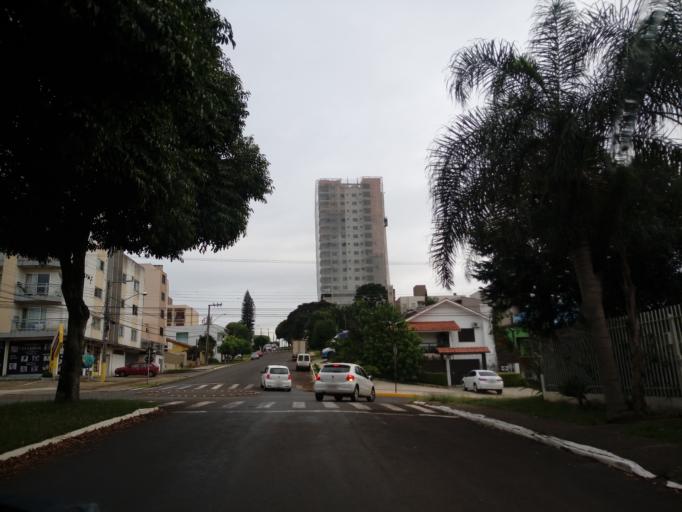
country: BR
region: Santa Catarina
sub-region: Chapeco
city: Chapeco
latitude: -27.0948
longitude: -52.6073
